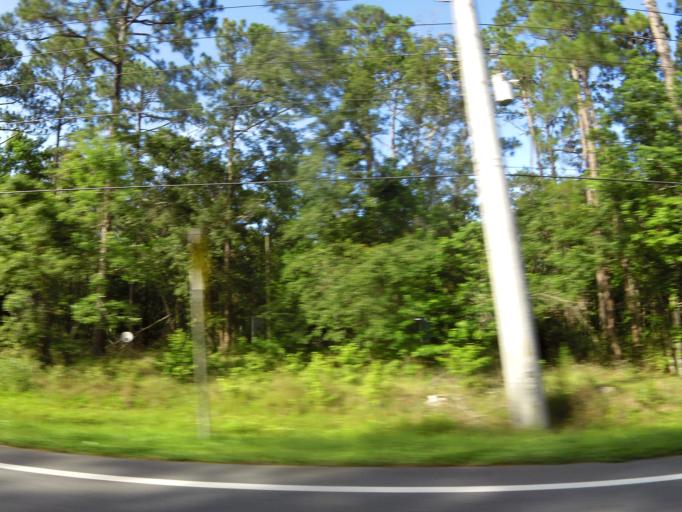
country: US
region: Florida
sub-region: Clay County
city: Green Cove Springs
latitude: 30.0132
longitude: -81.5588
